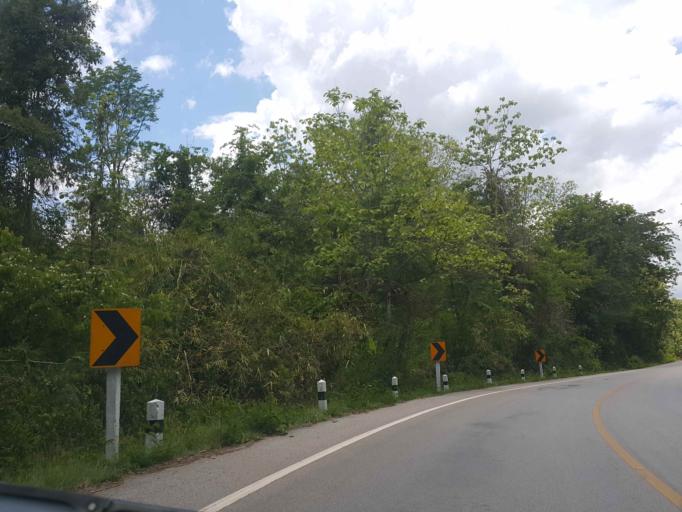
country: TH
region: Nan
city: Wiang Sa
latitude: 18.5182
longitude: 100.5897
